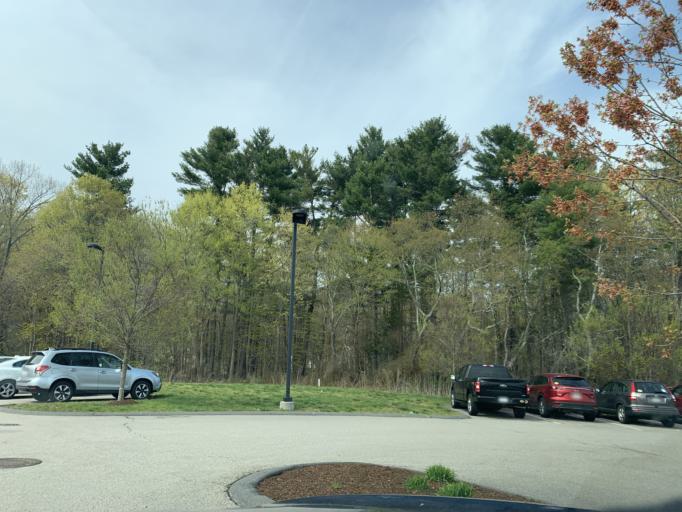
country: US
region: Massachusetts
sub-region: Norfolk County
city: Norwood
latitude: 42.2155
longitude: -71.1939
